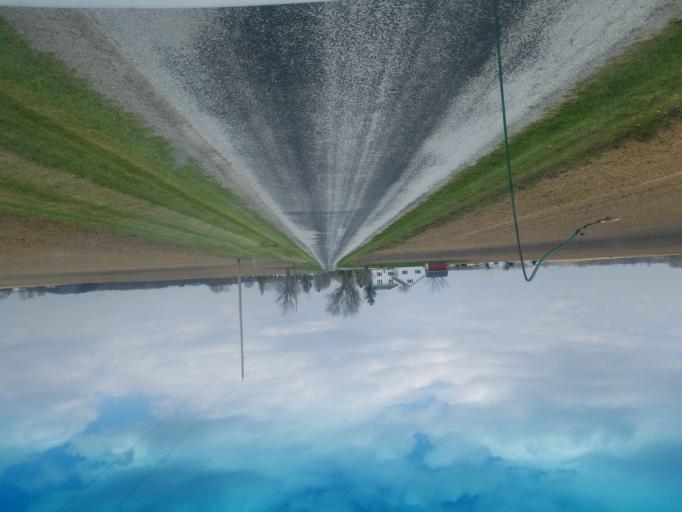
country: US
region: Ohio
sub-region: Wyandot County
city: Upper Sandusky
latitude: 40.9444
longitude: -83.2309
